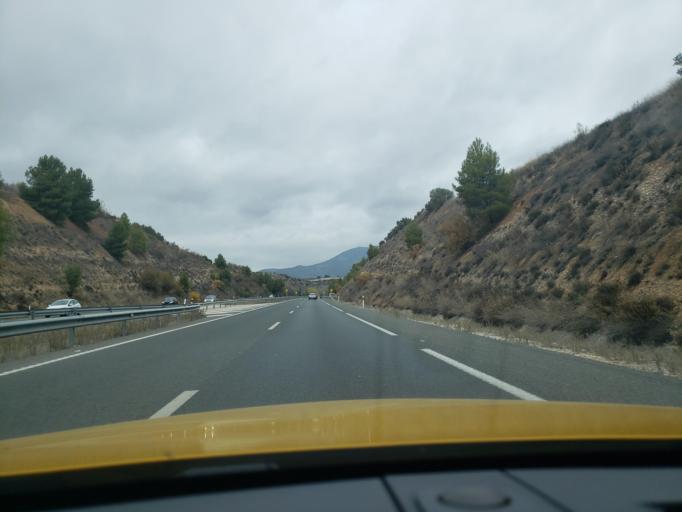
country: ES
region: Andalusia
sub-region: Provincia de Granada
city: Calicasas
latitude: 37.2965
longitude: -3.6571
